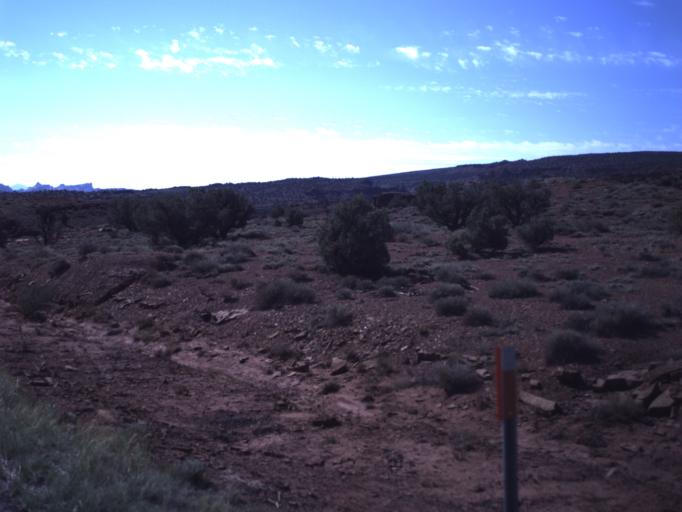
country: US
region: Utah
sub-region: Wayne County
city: Loa
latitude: 38.3184
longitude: -111.3120
